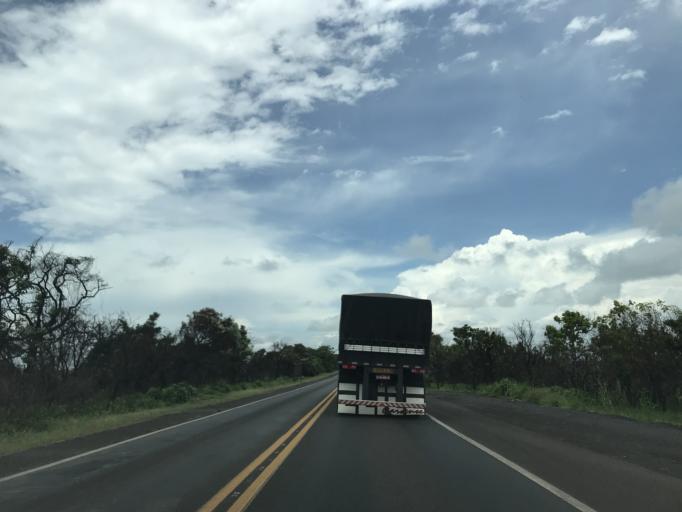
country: BR
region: Minas Gerais
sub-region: Frutal
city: Frutal
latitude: -19.7242
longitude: -48.9757
